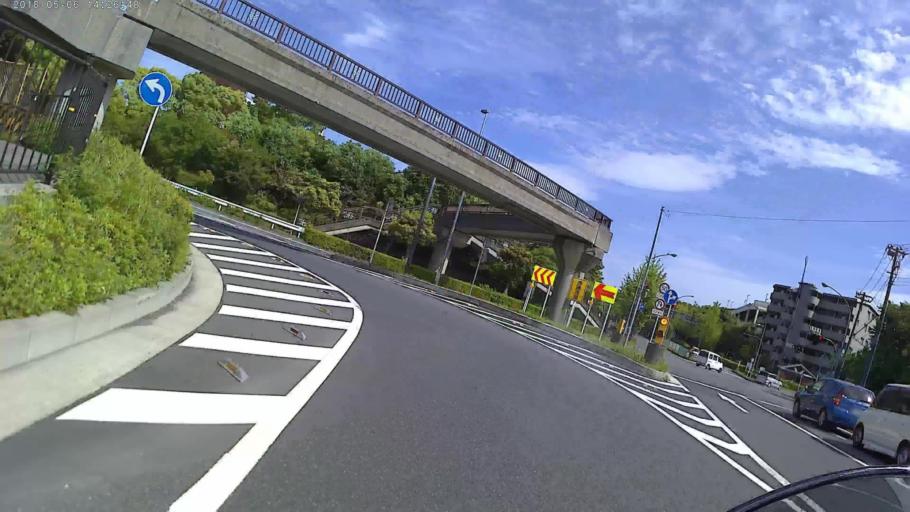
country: JP
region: Kanagawa
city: Yokohama
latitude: 35.4325
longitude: 139.6645
